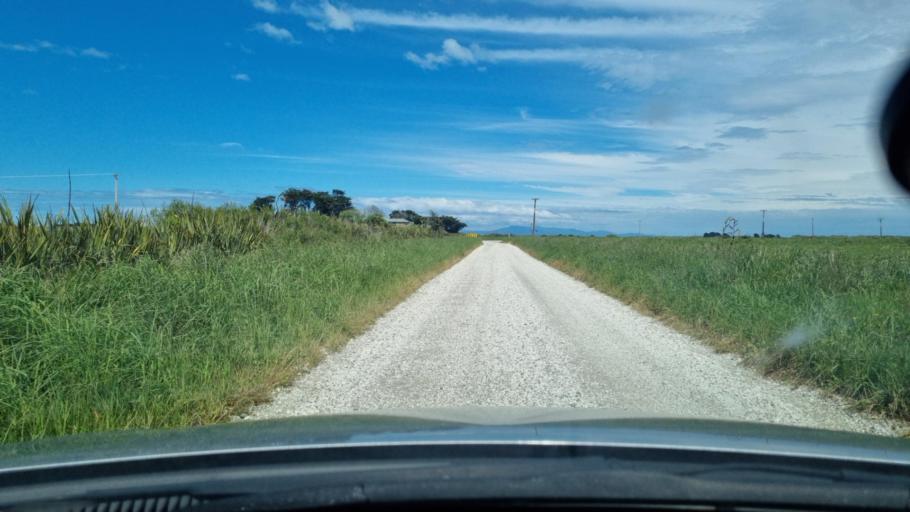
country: NZ
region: Southland
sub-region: Invercargill City
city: Invercargill
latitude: -46.3893
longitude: 168.2611
